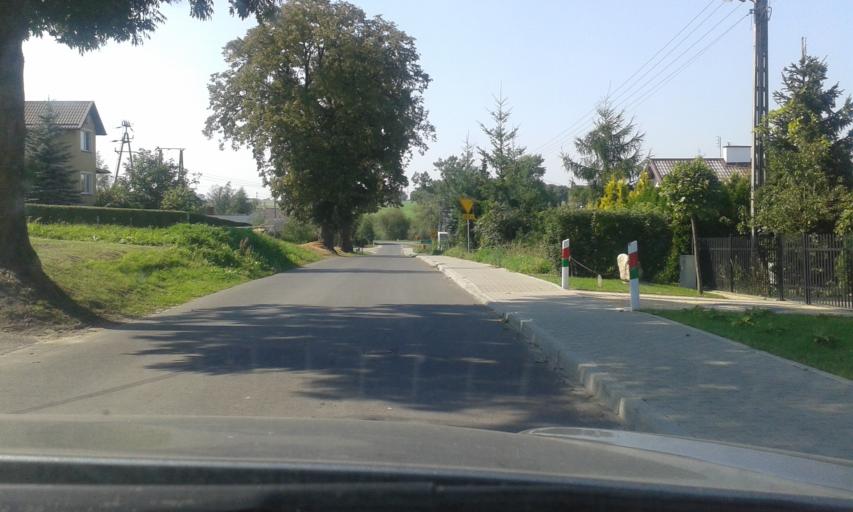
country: PL
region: Kujawsko-Pomorskie
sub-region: Powiat swiecki
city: Nowe
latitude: 53.6737
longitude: 18.7284
